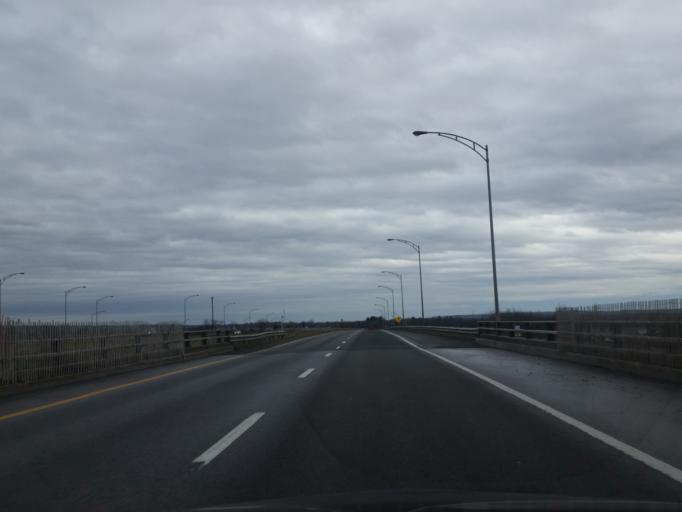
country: CA
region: Quebec
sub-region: Outaouais
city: Gatineau
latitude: 45.5132
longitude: -75.5623
